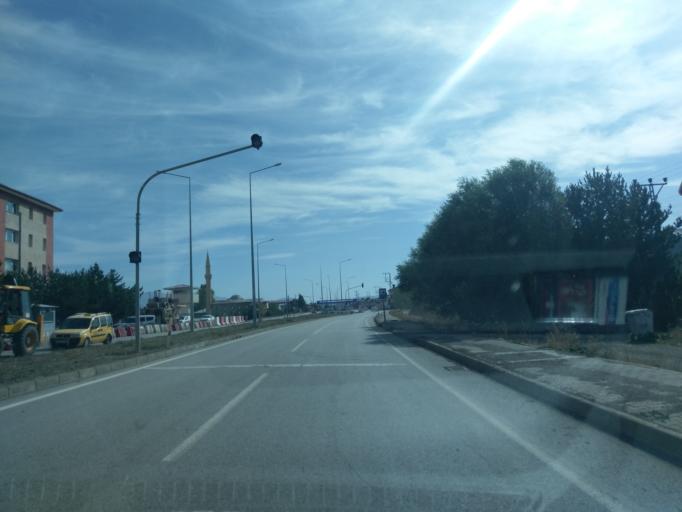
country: TR
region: Sivas
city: Imranli
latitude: 39.8717
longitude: 38.1093
